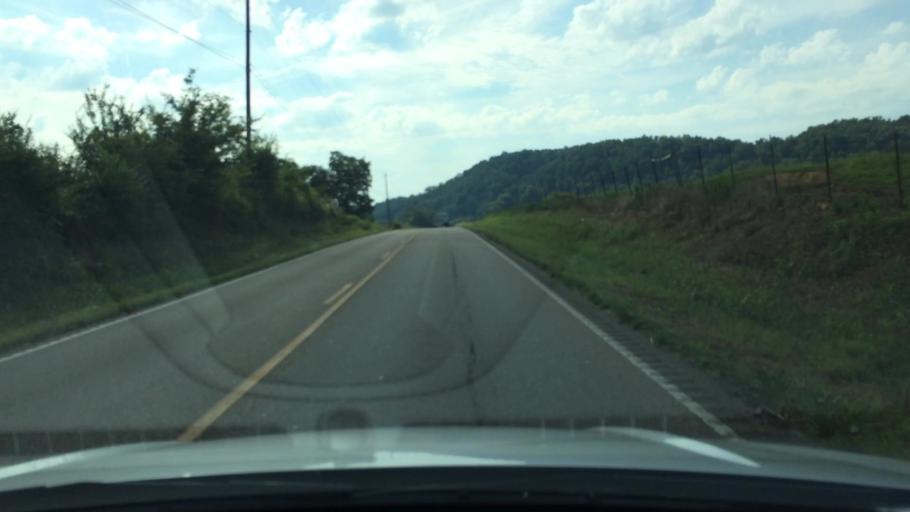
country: US
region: Tennessee
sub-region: Sevier County
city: Seymour
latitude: 35.9154
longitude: -83.6385
